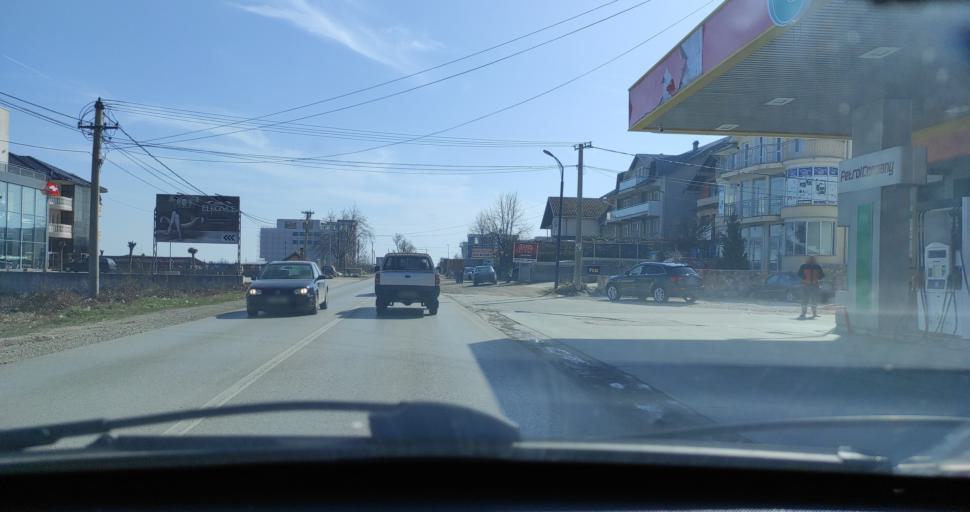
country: XK
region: Pec
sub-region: Komuna e Pejes
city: Peje
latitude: 42.6371
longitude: 20.2988
